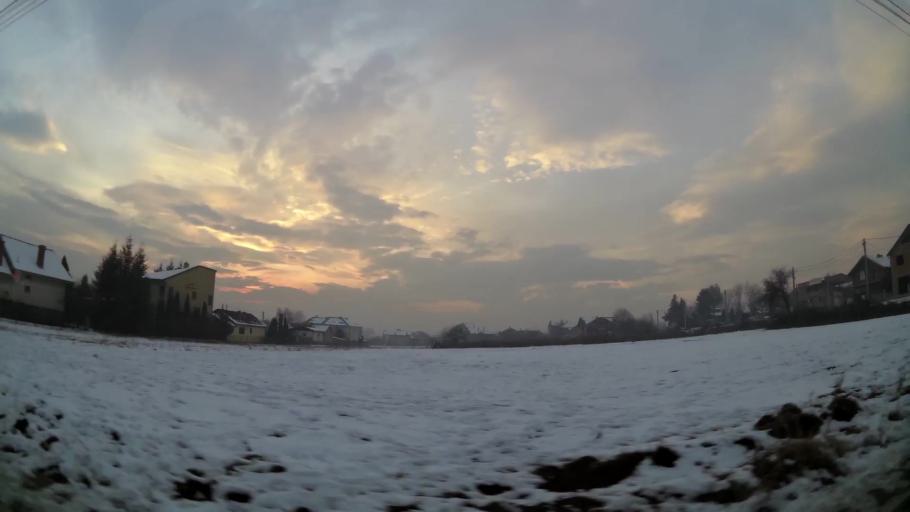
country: MK
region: Suto Orizari
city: Suto Orizare
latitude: 42.0389
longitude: 21.4076
